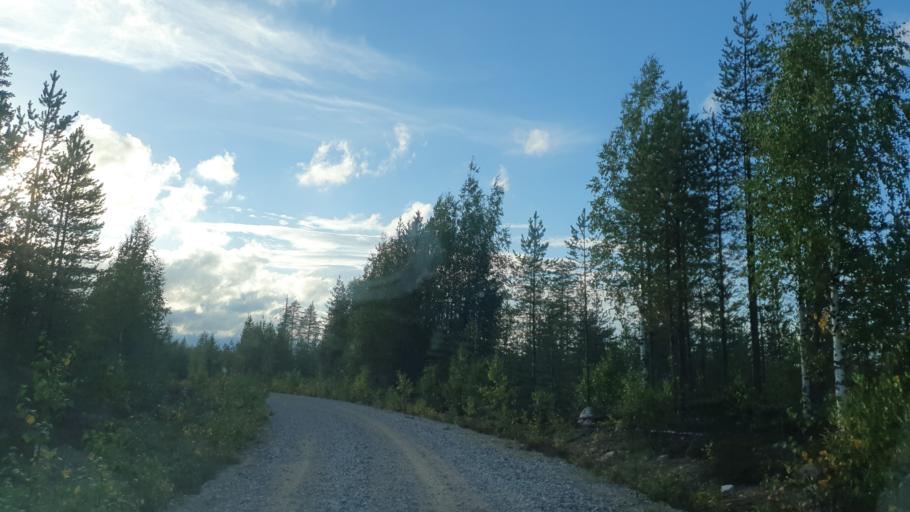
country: FI
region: Kainuu
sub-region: Kehys-Kainuu
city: Kuhmo
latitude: 64.3345
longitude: 30.0075
